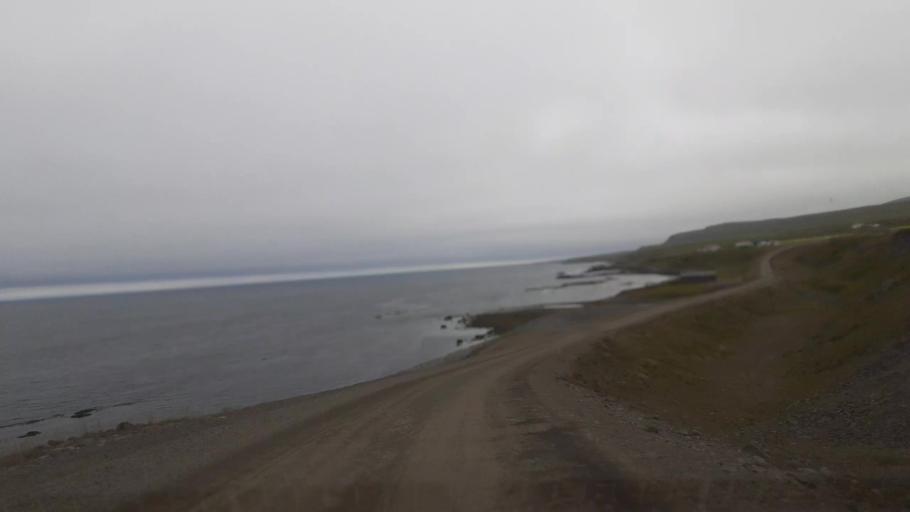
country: IS
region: Northwest
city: Saudarkrokur
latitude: 65.5263
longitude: -20.9640
